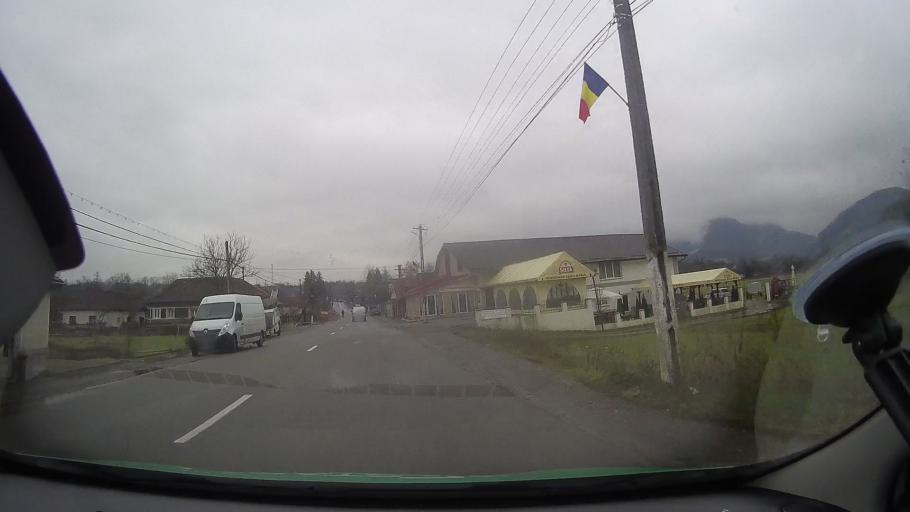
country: RO
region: Arad
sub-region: Comuna Varfurile
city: Varfurile
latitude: 46.3084
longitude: 22.5224
